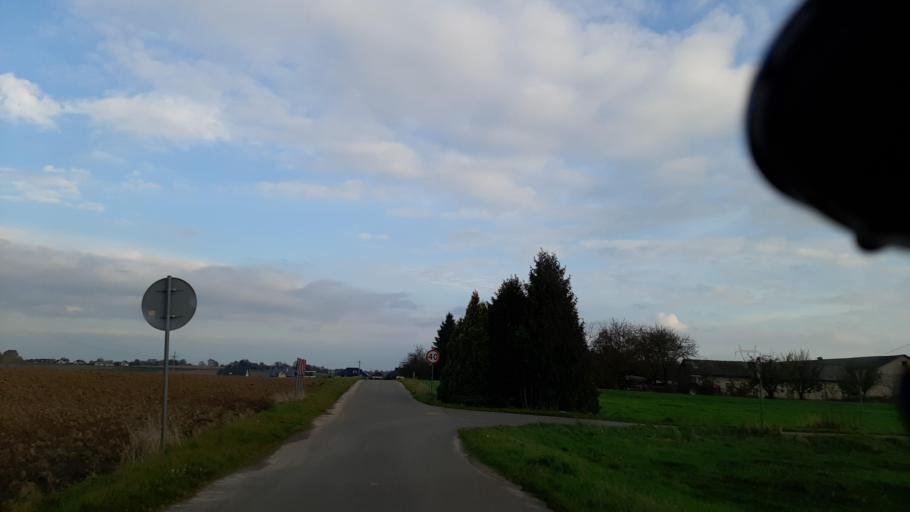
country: PL
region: Lublin Voivodeship
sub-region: Powiat lubelski
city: Garbow
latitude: 51.3425
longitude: 22.3211
